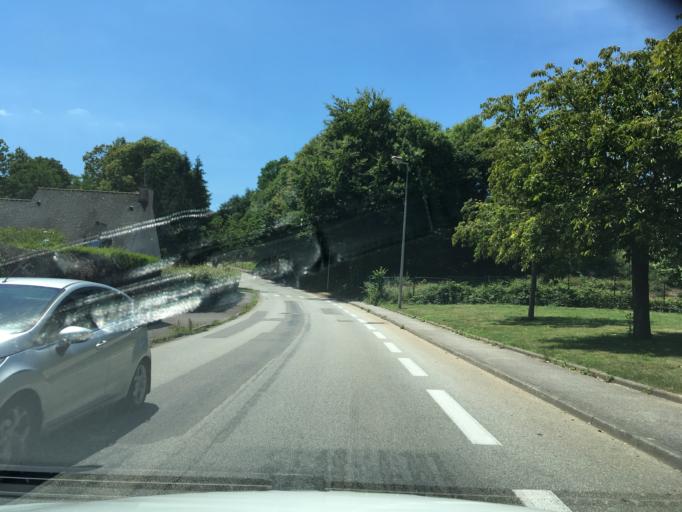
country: FR
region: Brittany
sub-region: Departement du Finistere
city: Quimper
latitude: 47.9953
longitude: -4.1375
